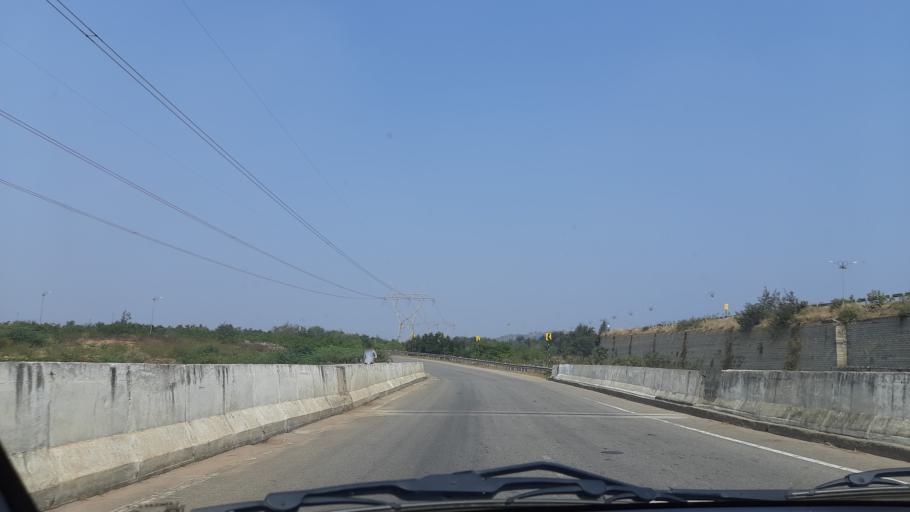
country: IN
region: Telangana
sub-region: Rangareddi
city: Lal Bahadur Nagar
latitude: 17.3136
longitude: 78.6564
